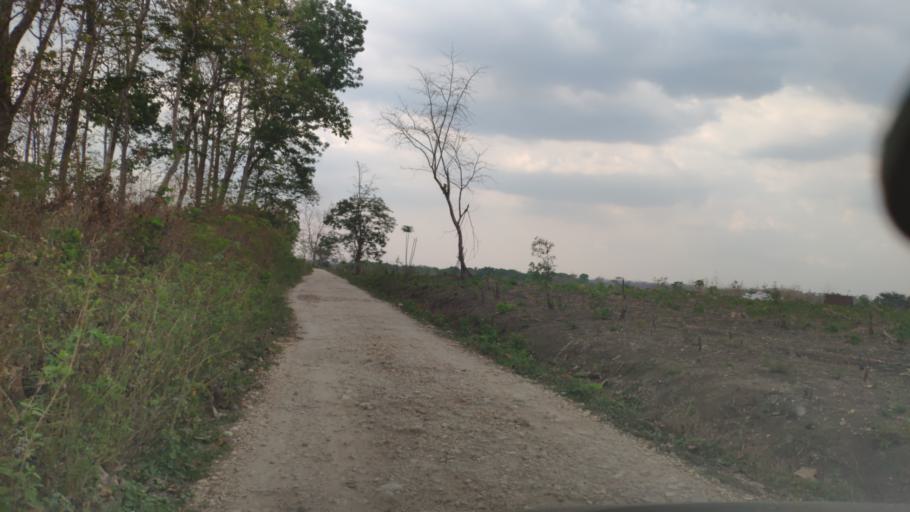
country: ID
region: Central Java
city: Randublatung
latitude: -7.2859
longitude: 111.2952
